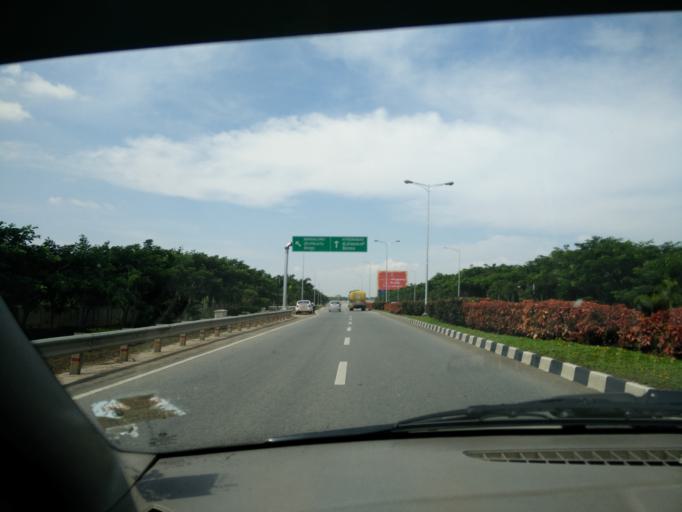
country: IN
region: Karnataka
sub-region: Bangalore Rural
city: Devanhalli
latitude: 13.1981
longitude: 77.6711
